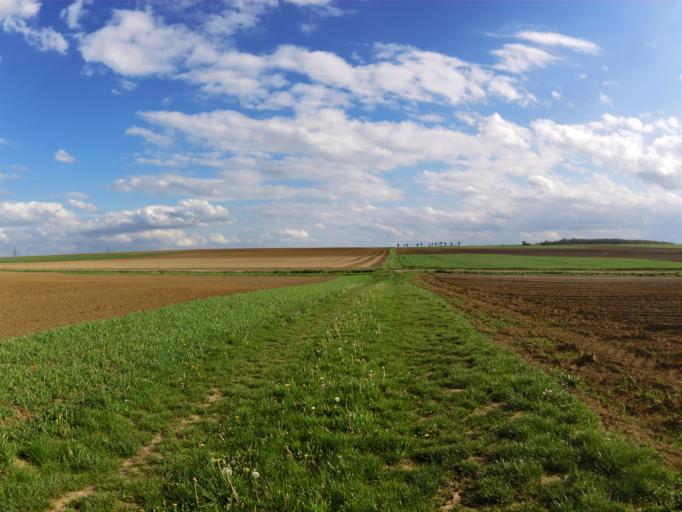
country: DE
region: Bavaria
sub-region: Regierungsbezirk Unterfranken
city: Oberpleichfeld
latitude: 49.8603
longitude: 10.0754
